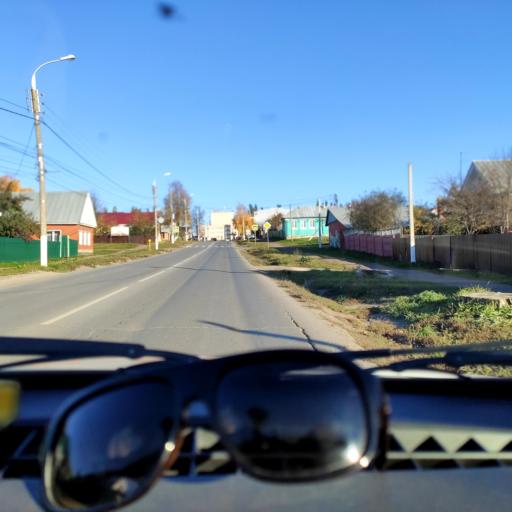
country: RU
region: Bashkortostan
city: Blagoveshchensk
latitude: 55.0432
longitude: 55.9604
